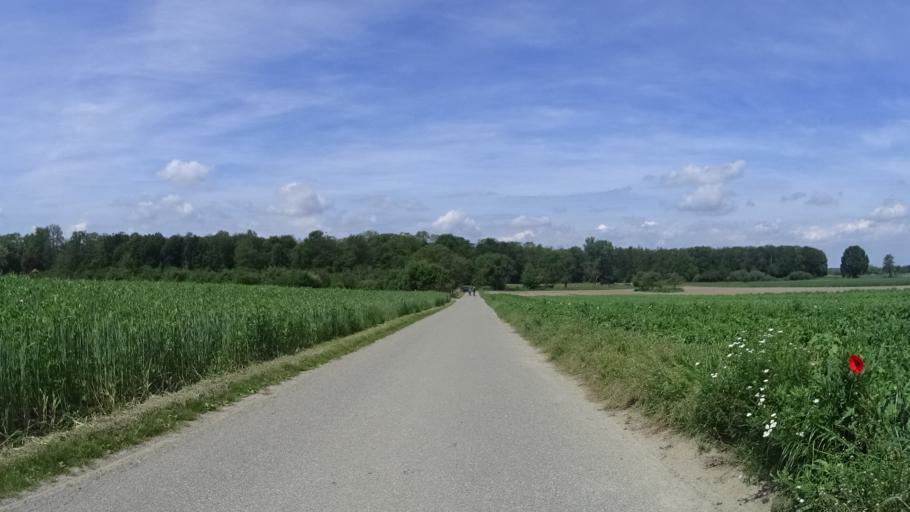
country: DE
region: Baden-Wuerttemberg
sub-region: Freiburg Region
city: Meissenheim
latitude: 48.4312
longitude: 7.8003
